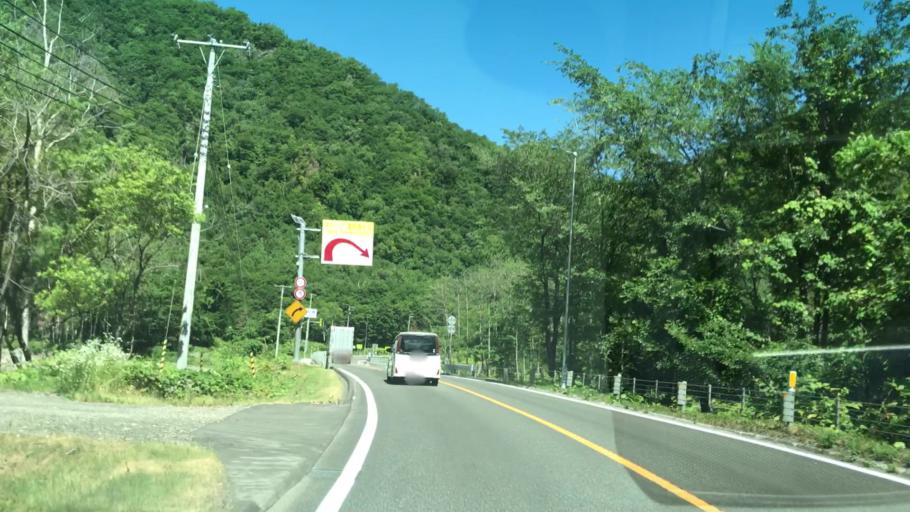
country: JP
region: Hokkaido
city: Shimo-furano
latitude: 42.9157
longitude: 142.5871
